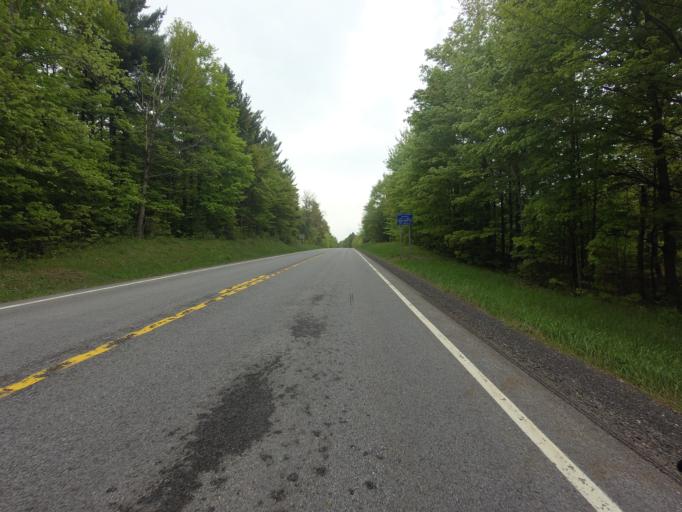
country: US
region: New York
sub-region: St. Lawrence County
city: Hannawa Falls
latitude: 44.6484
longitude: -74.7715
